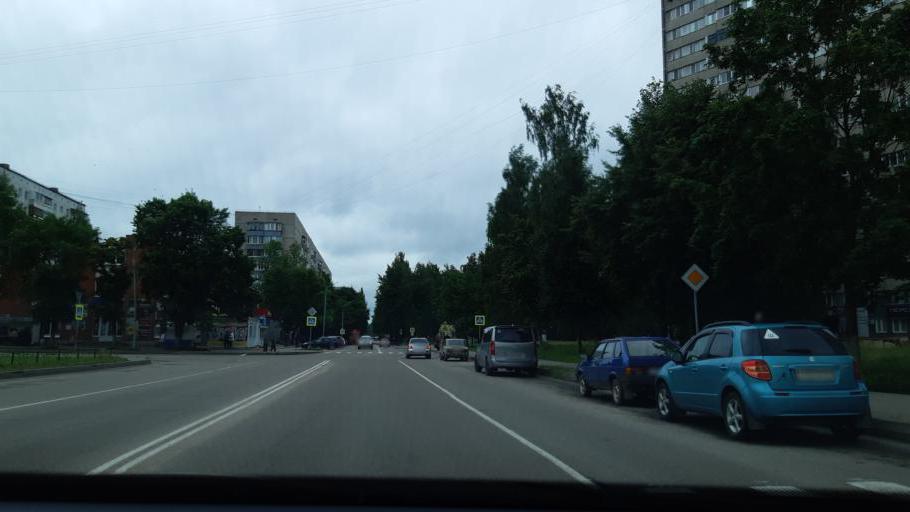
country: RU
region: Smolensk
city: Desnogorsk
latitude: 54.1537
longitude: 33.2885
